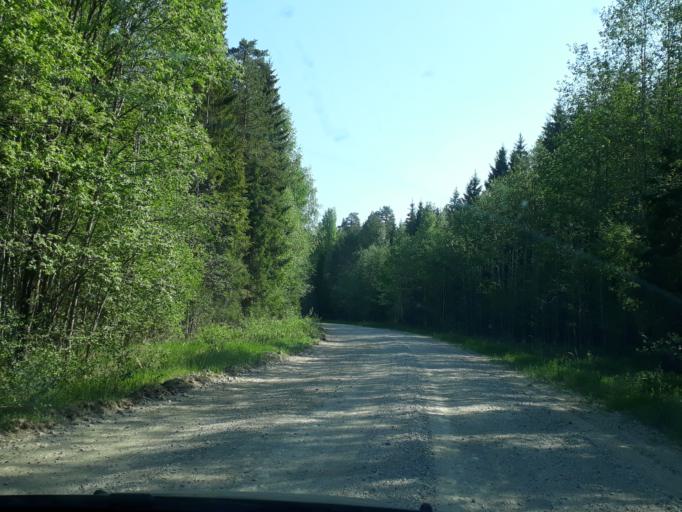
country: LV
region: Ligatne
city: Ligatne
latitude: 57.2761
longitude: 25.0697
